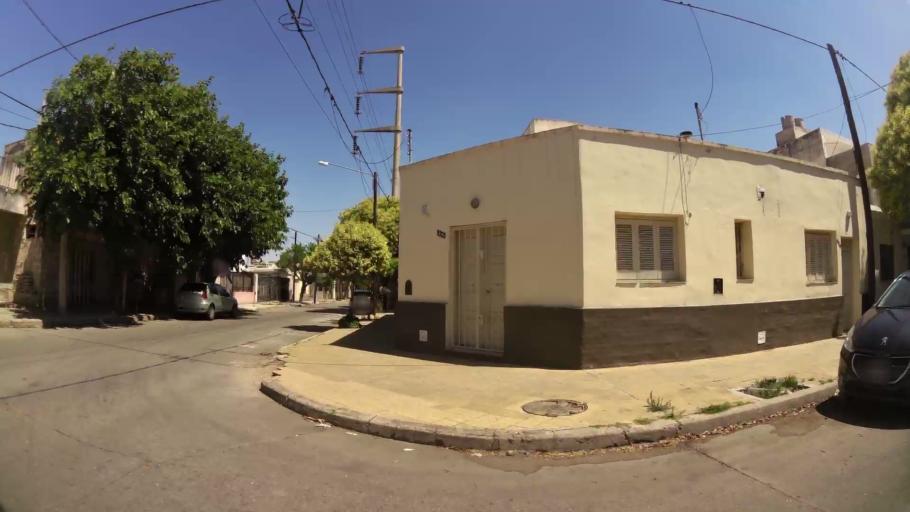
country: AR
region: Cordoba
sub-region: Departamento de Capital
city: Cordoba
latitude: -31.3817
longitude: -64.1977
